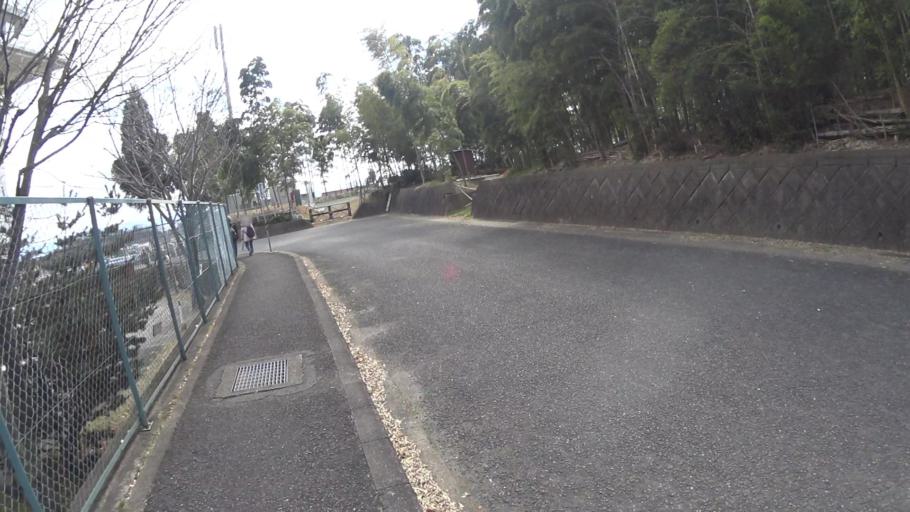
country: JP
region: Kyoto
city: Muko
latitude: 34.9534
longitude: 135.6909
